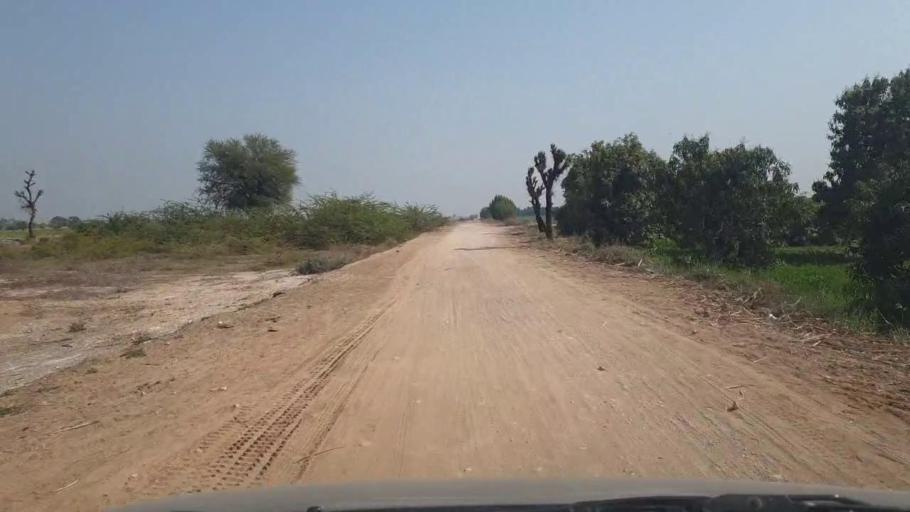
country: PK
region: Sindh
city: Digri
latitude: 25.2387
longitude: 69.1459
